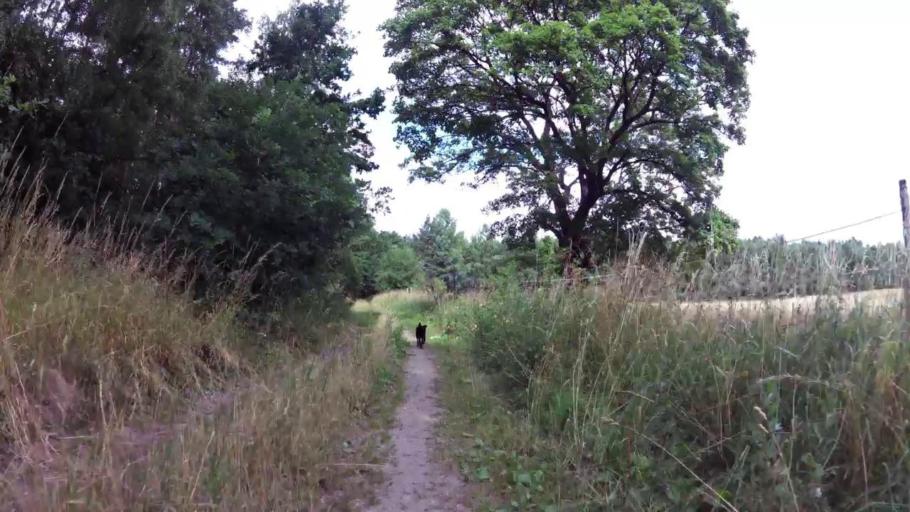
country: PL
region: West Pomeranian Voivodeship
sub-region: Powiat lobeski
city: Lobez
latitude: 53.6042
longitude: 15.6631
